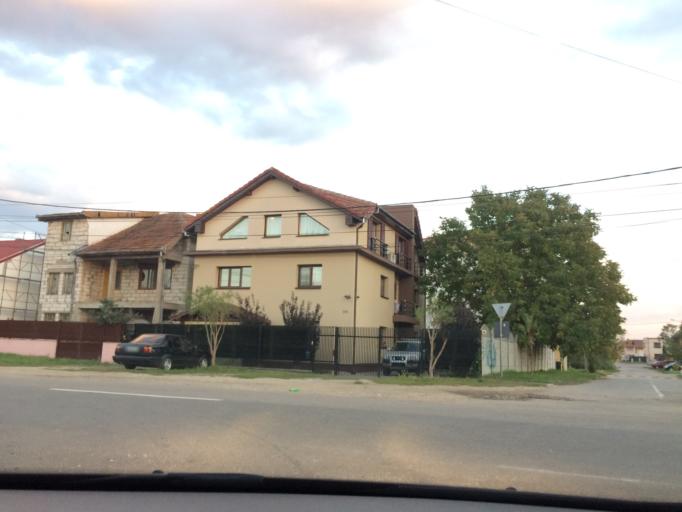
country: RO
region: Timis
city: Timisoara
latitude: 45.7569
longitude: 21.1941
